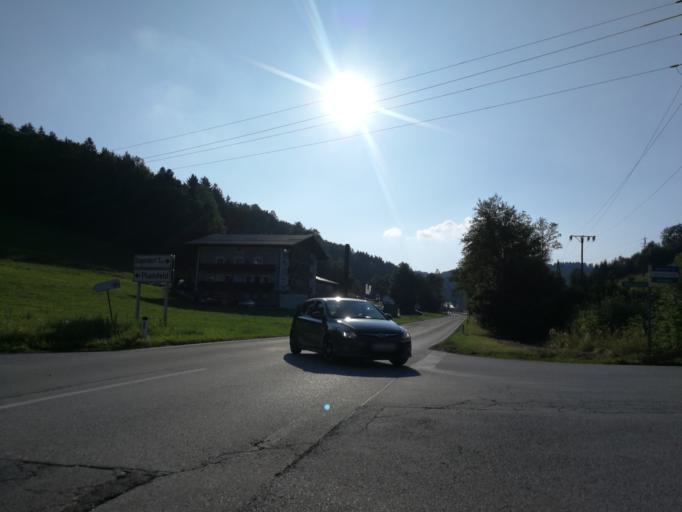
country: AT
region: Salzburg
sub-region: Politischer Bezirk Salzburg-Umgebung
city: Plainfeld
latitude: 47.8331
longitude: 13.1819
